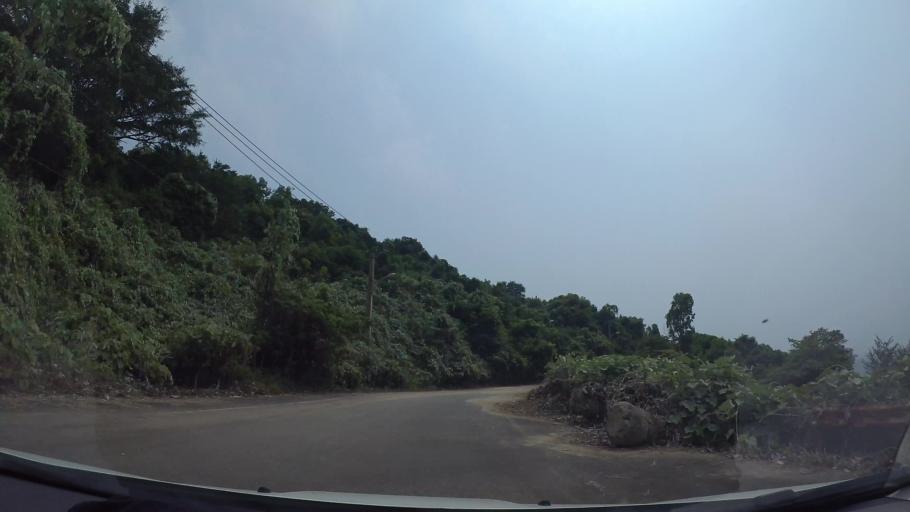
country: VN
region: Da Nang
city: Son Tra
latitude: 16.1015
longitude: 108.3018
